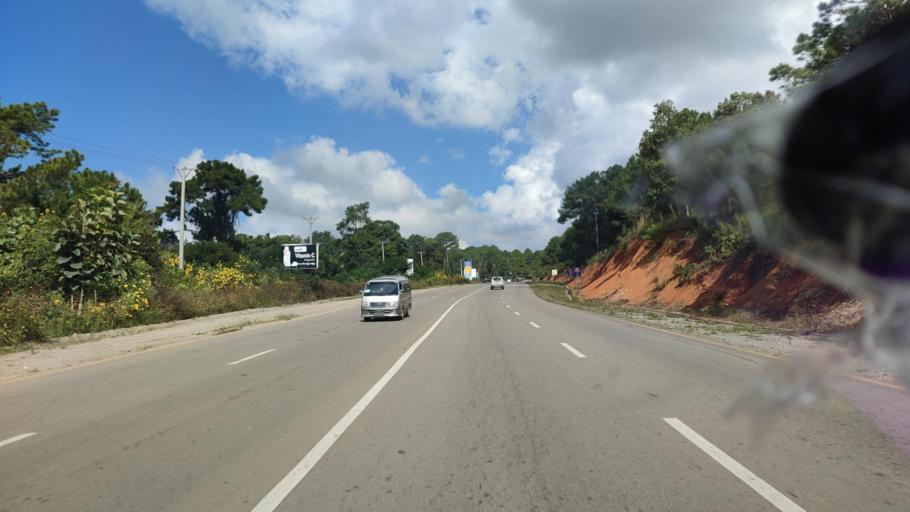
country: MM
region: Shan
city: Taunggyi
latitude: 20.6481
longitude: 96.5917
